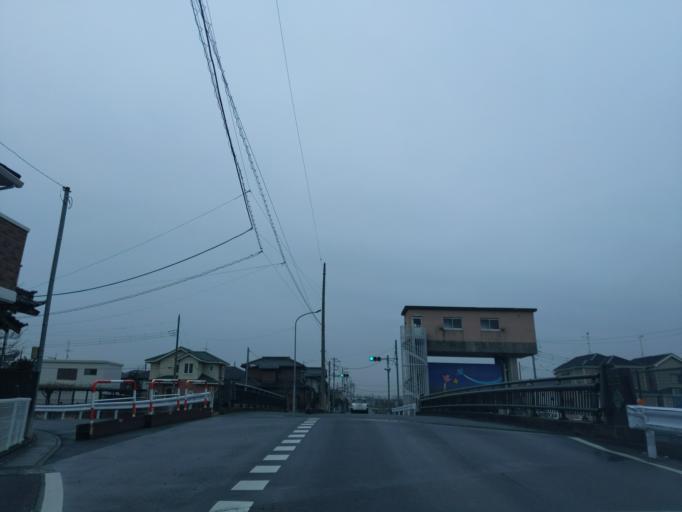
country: JP
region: Saitama
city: Koshigaya
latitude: 35.8607
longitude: 139.7645
